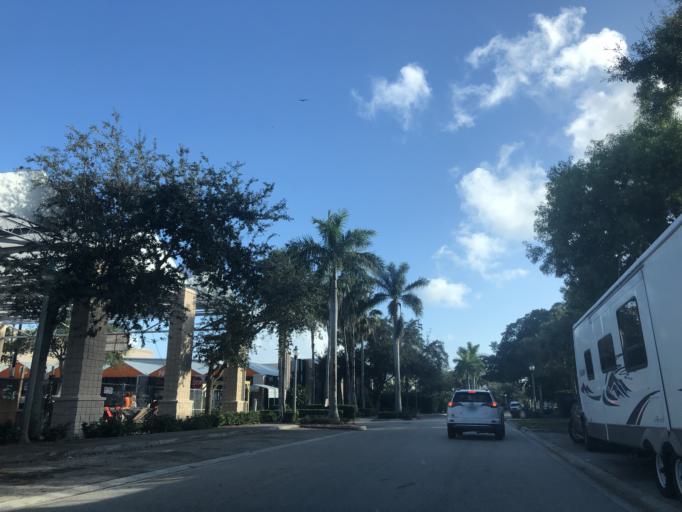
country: US
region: Florida
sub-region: Palm Beach County
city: West Palm Beach
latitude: 26.7228
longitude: -80.0802
